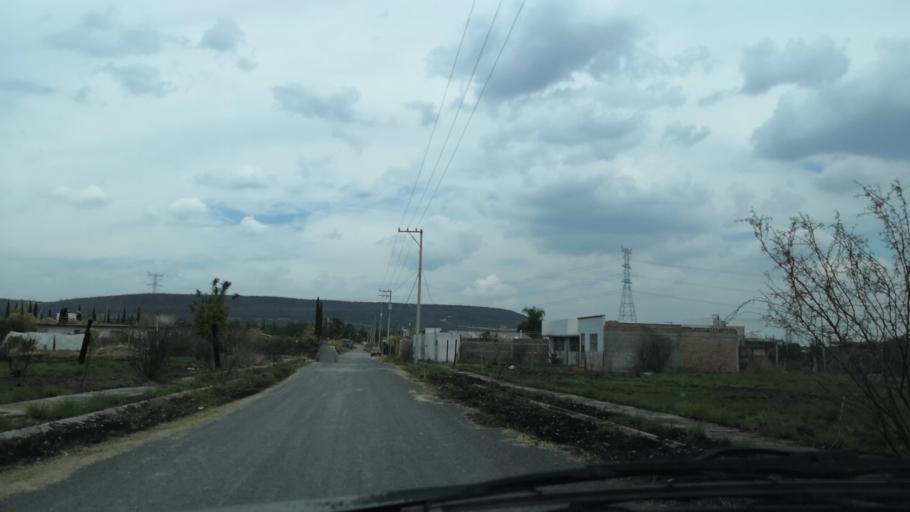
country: MX
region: Guanajuato
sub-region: San Francisco del Rincon
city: Barrio de Guadalupe del Mezquitillo
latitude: 20.9243
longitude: -101.7524
